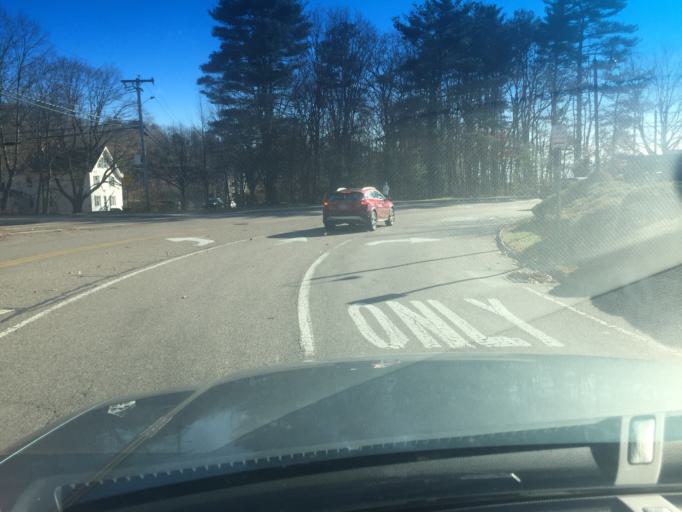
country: US
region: Massachusetts
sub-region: Norfolk County
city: Franklin
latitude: 42.0914
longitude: -71.4229
